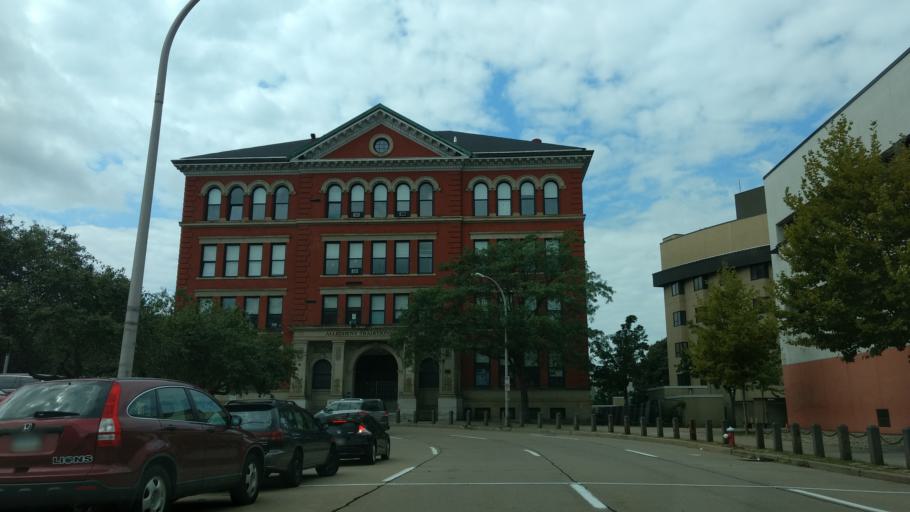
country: US
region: Pennsylvania
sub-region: Allegheny County
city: Pittsburgh
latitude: 40.4537
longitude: -80.0075
